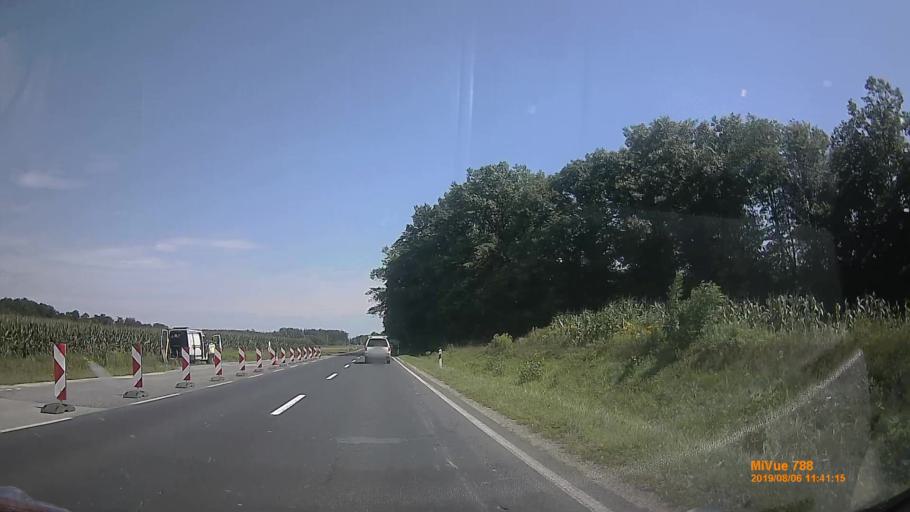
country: HU
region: Vas
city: Kormend
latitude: 46.9883
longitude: 16.5283
